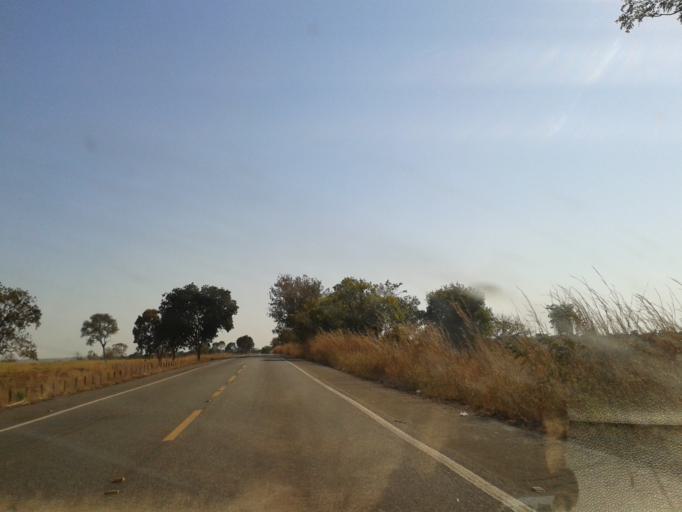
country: BR
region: Goias
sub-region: Mozarlandia
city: Mozarlandia
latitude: -14.8770
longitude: -50.5527
